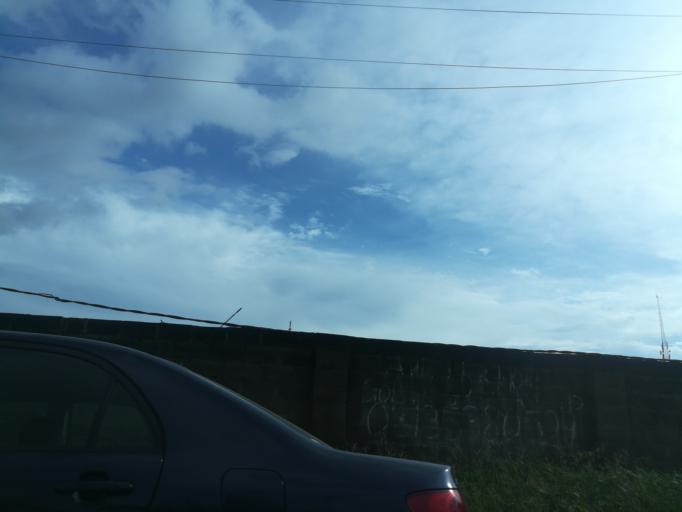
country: NG
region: Lagos
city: Ikeja
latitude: 6.6204
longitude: 3.3556
